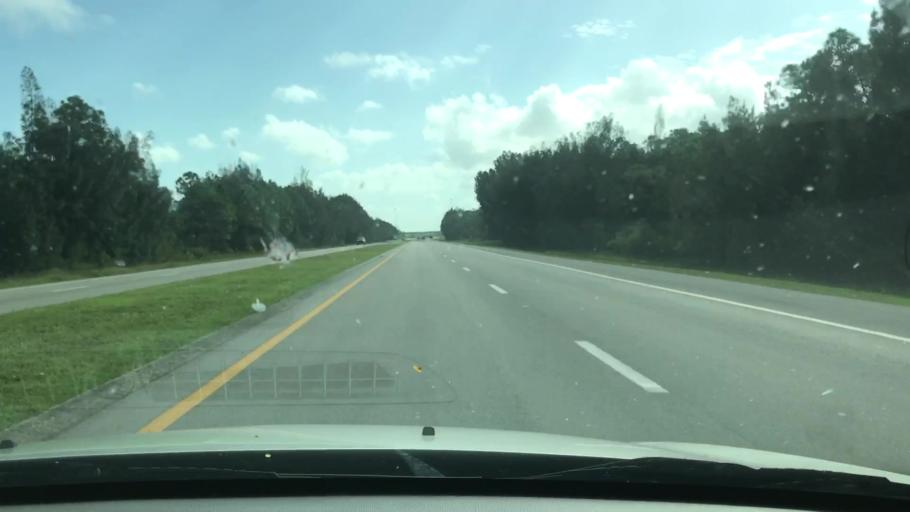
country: US
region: Florida
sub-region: Charlotte County
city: Charlotte Park
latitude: 26.8583
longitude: -81.9834
